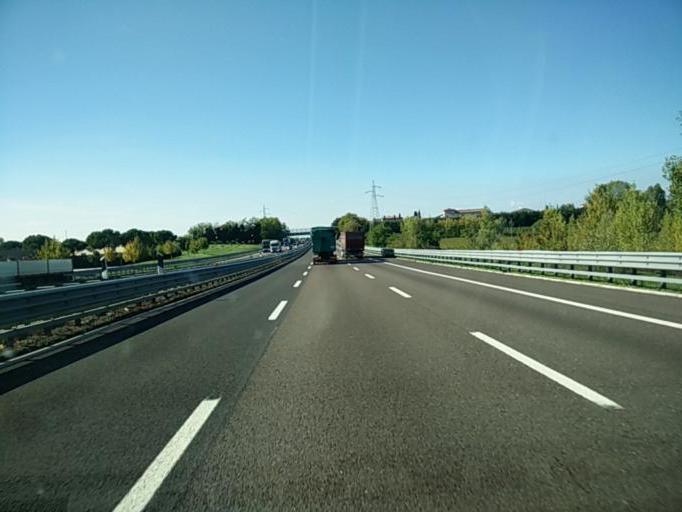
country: IT
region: Veneto
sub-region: Provincia di Verona
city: Peschiera del Garda
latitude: 45.4308
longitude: 10.6647
